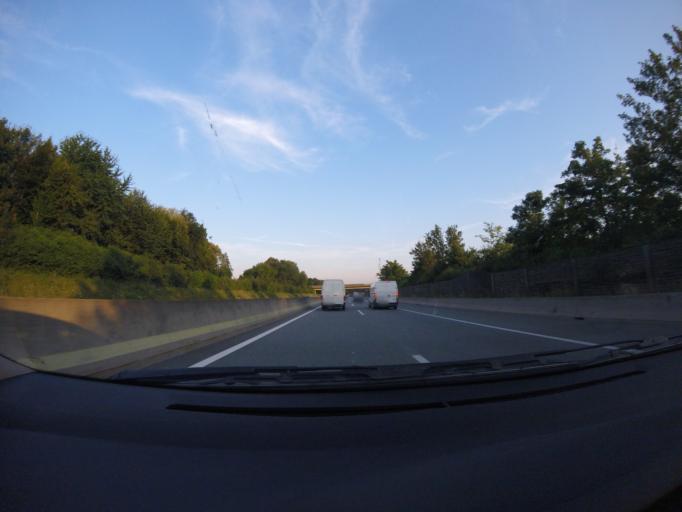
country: AT
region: Styria
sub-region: Politischer Bezirk Hartberg-Fuerstenfeld
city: Sebersdorf
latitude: 47.1888
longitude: 15.9964
